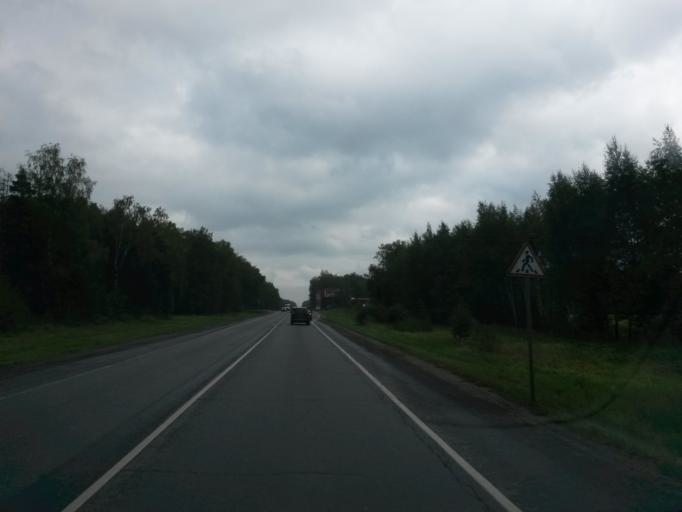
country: RU
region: Moskovskaya
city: Klimovsk
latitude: 55.3312
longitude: 37.6081
